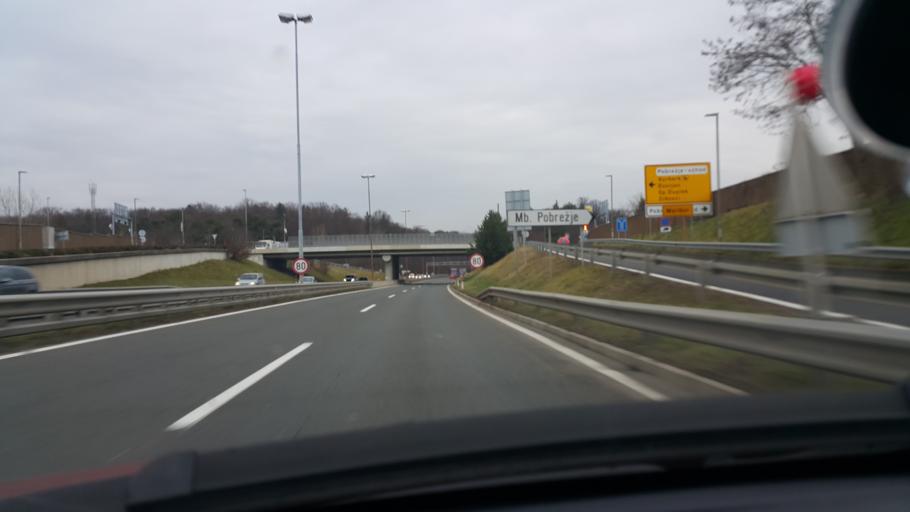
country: SI
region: Maribor
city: Maribor
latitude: 46.5487
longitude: 15.6616
